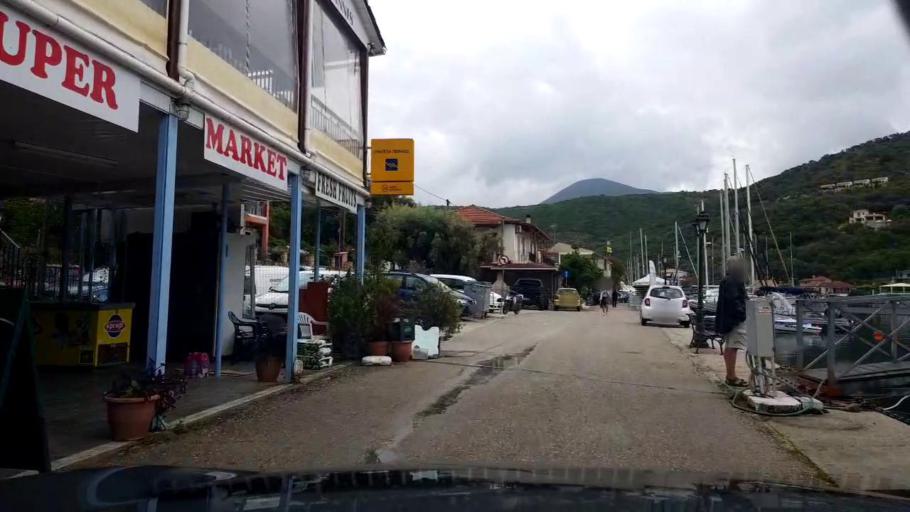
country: GR
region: Ionian Islands
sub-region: Lefkada
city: Nidri
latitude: 38.6221
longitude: 20.6823
